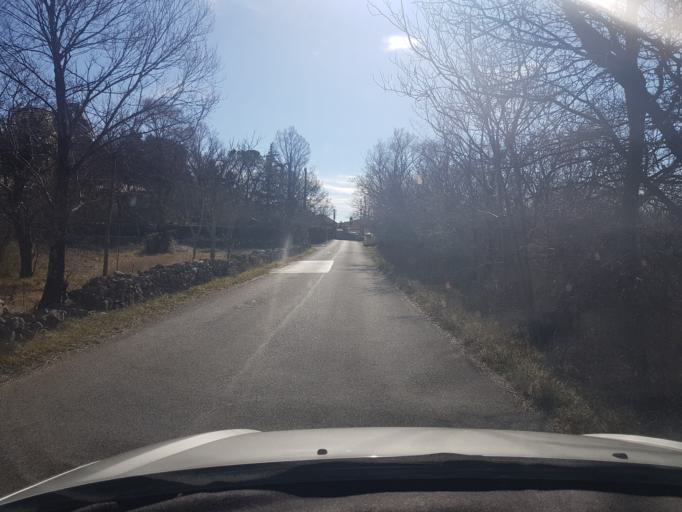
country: IT
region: Friuli Venezia Giulia
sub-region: Provincia di Trieste
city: Santa Croce
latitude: 45.7426
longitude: 13.7113
